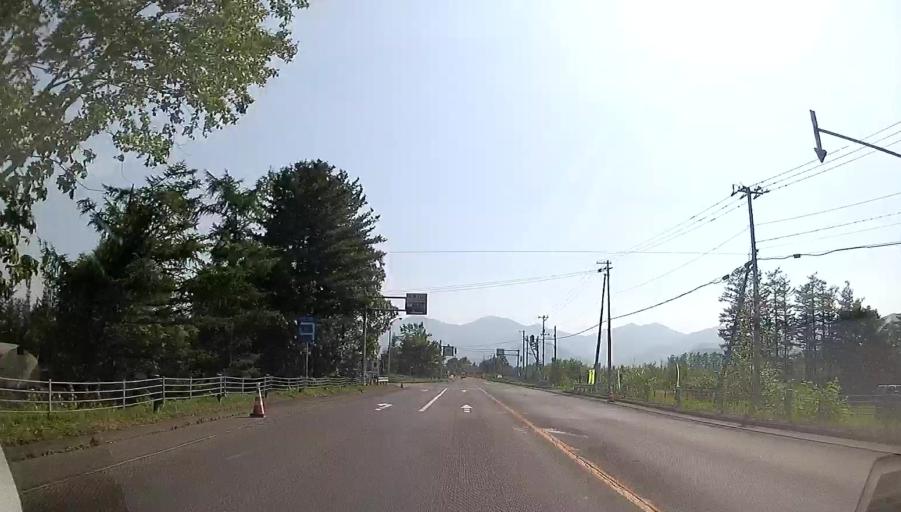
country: JP
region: Hokkaido
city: Otofuke
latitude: 42.9973
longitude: 142.8566
